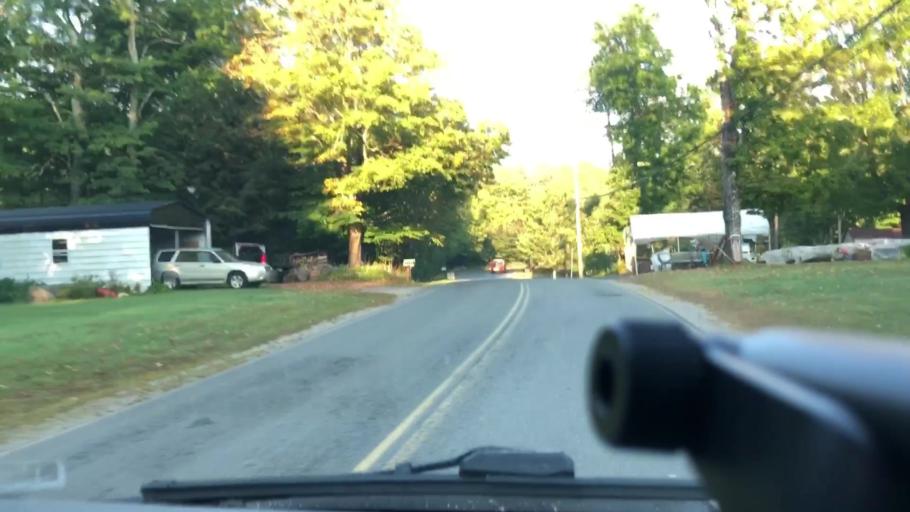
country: US
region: Massachusetts
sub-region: Franklin County
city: Ashfield
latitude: 42.5084
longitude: -72.8292
